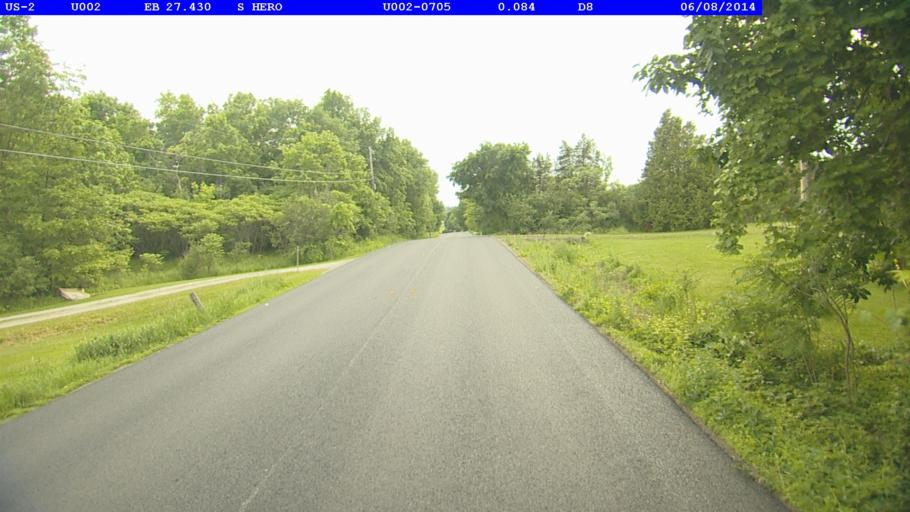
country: US
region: New York
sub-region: Clinton County
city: Cumberland Head
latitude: 44.6791
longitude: -73.3167
